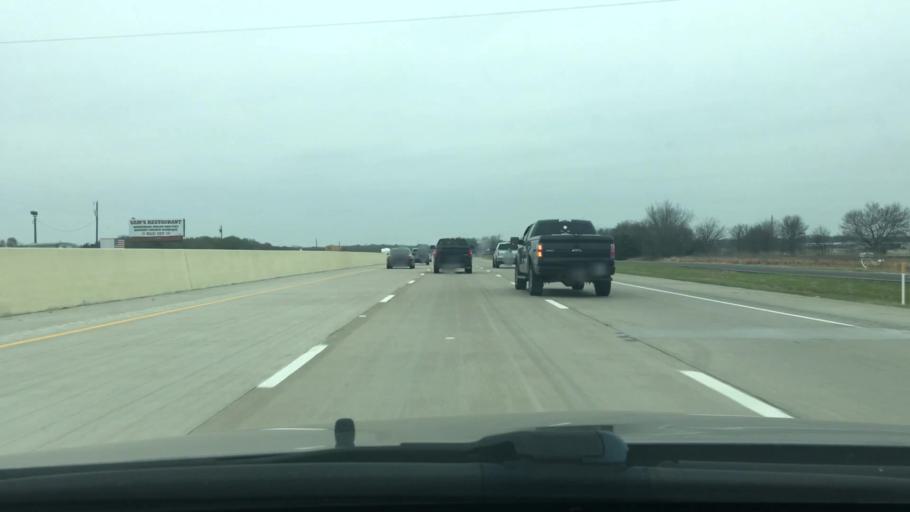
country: US
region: Texas
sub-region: Navarro County
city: Corsicana
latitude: 31.9742
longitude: -96.4228
